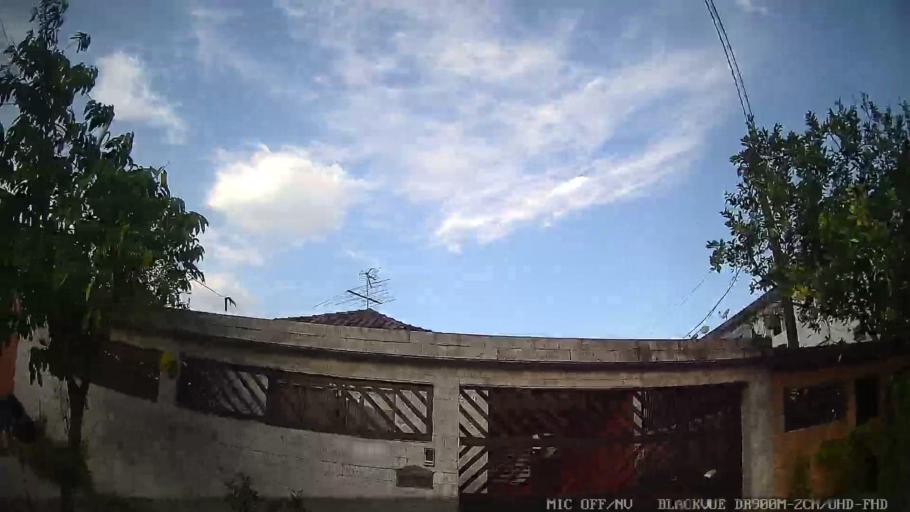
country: BR
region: Sao Paulo
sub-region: Cubatao
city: Cubatao
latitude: -23.8931
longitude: -46.4235
